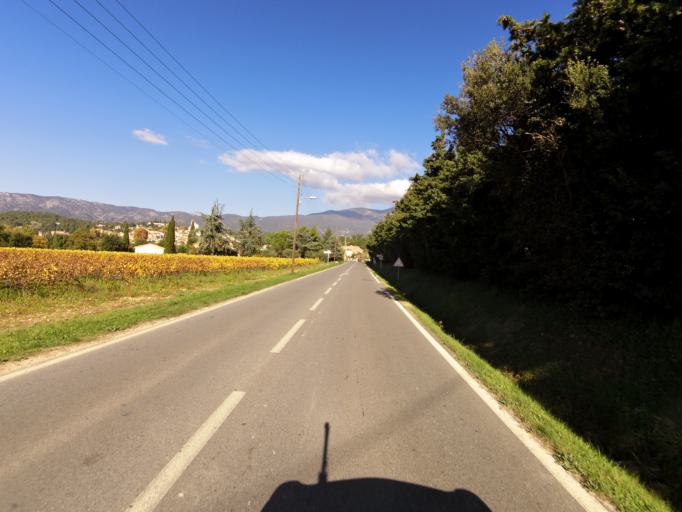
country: FR
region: Provence-Alpes-Cote d'Azur
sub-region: Departement du Vaucluse
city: Bedoin
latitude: 44.1170
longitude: 5.1779
